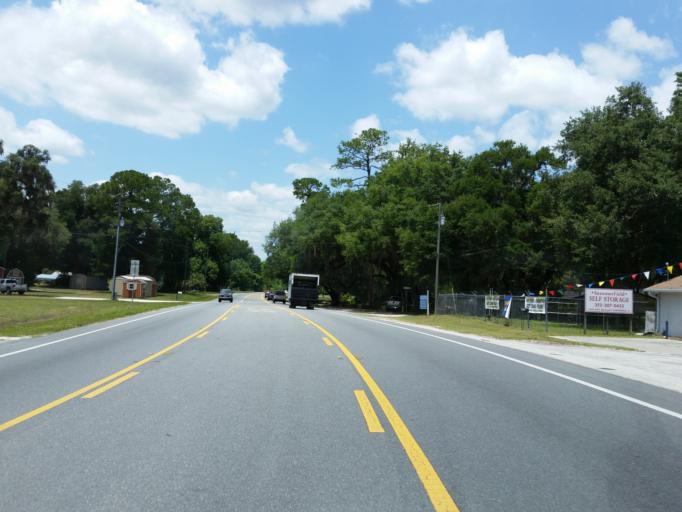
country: US
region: Florida
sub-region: Marion County
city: Belleview
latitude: 29.0118
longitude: -82.0417
